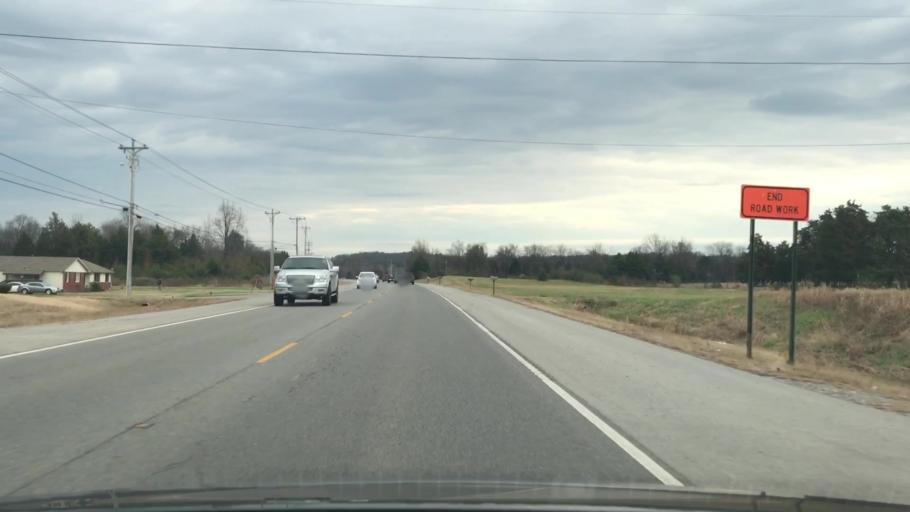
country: US
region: Tennessee
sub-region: Wilson County
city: Lebanon
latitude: 36.2541
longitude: -86.2453
